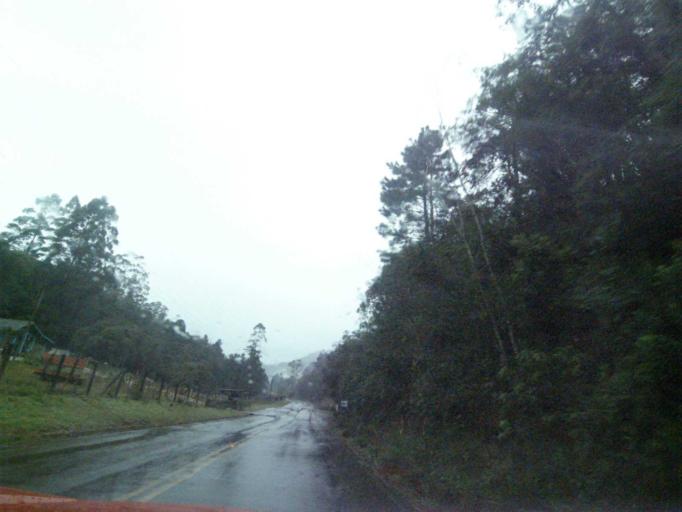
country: BR
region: Santa Catarina
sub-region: Anitapolis
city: Anitapolis
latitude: -27.8232
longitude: -49.0494
